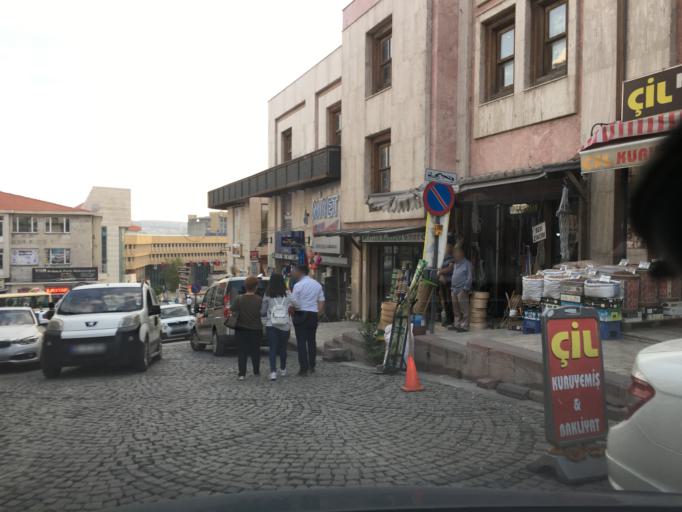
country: TR
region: Ankara
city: Cankaya
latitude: 39.9358
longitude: 32.8637
